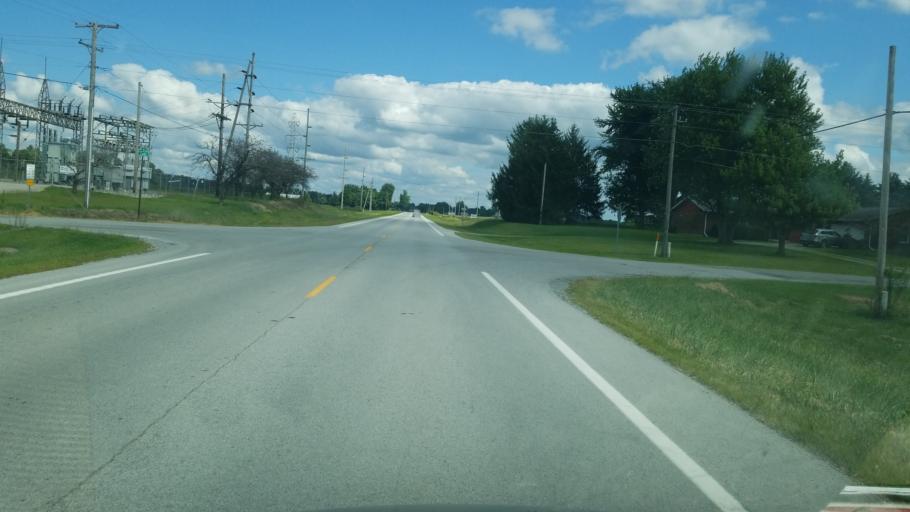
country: US
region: Ohio
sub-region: Allen County
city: Lima
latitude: 40.7643
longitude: -83.9945
